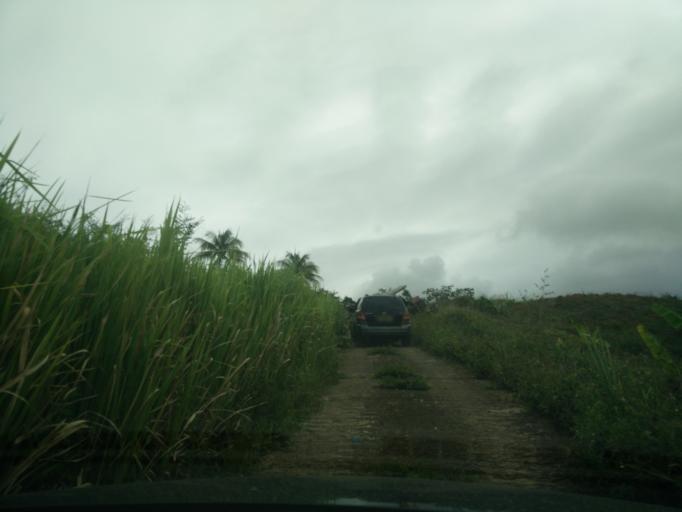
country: GP
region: Guadeloupe
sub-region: Guadeloupe
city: Capesterre-Belle-Eau
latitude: 16.1099
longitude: -61.6070
